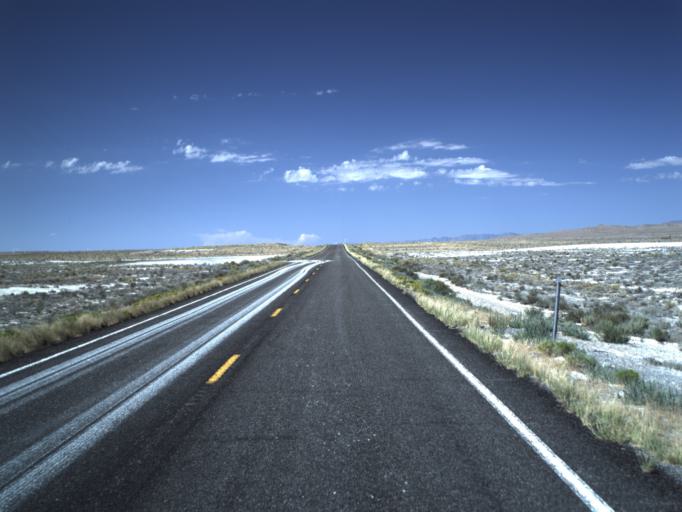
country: US
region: Utah
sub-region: Millard County
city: Delta
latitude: 39.1961
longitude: -112.9906
